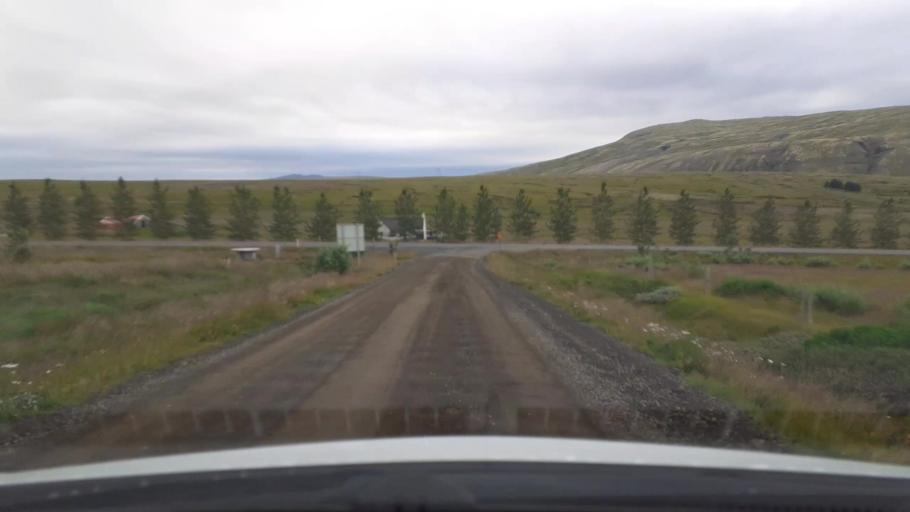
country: IS
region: Capital Region
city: Mosfellsbaer
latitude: 64.1896
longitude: -21.5374
